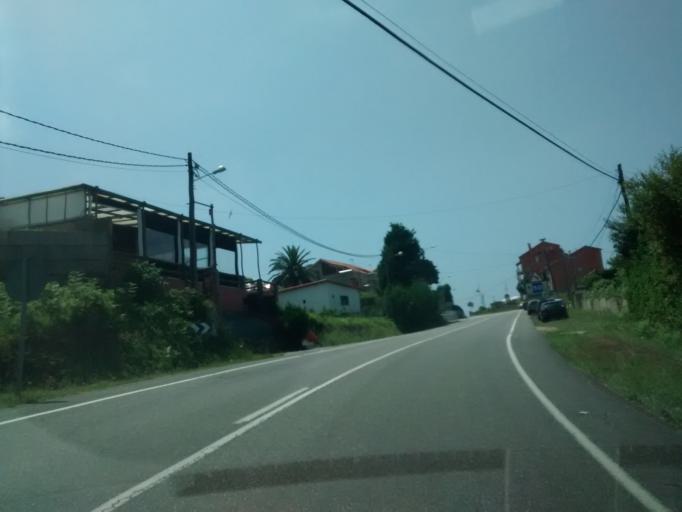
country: ES
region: Galicia
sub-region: Provincia de Pontevedra
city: Sanxenxo
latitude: 42.3942
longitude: -8.8438
